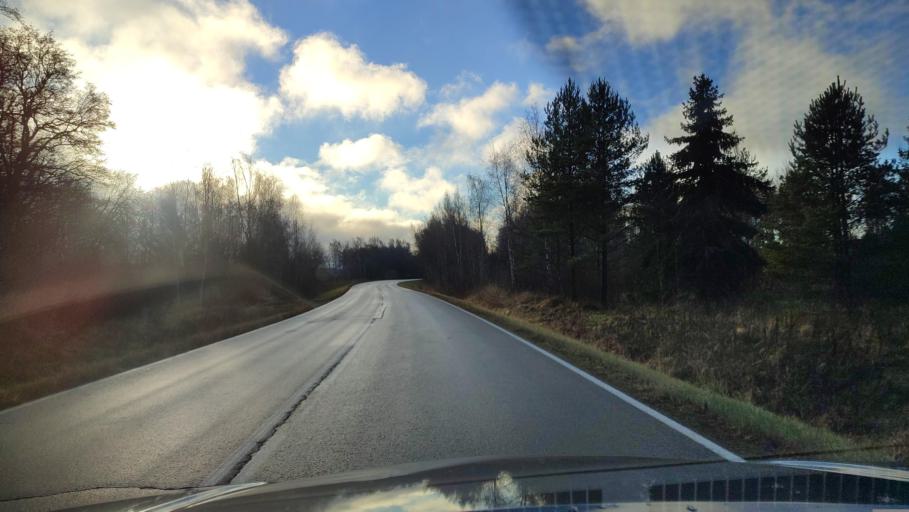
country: FI
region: Ostrobothnia
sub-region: Sydosterbotten
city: Kristinestad
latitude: 62.2867
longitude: 21.3775
